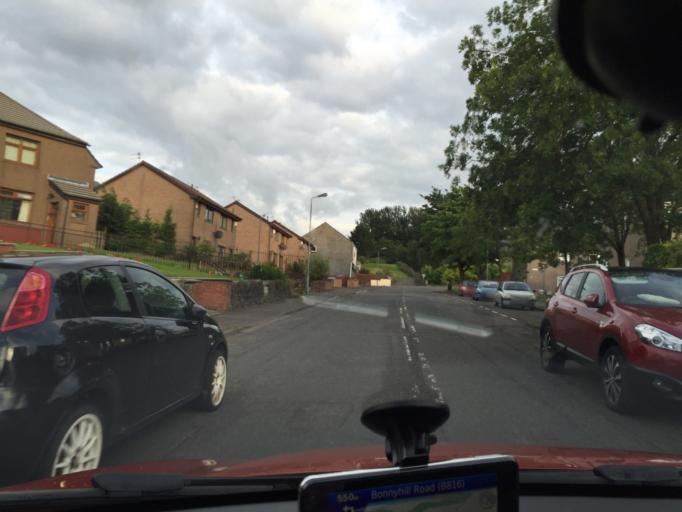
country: GB
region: Scotland
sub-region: Falkirk
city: Bonnybridge
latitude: 55.9940
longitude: -3.8773
